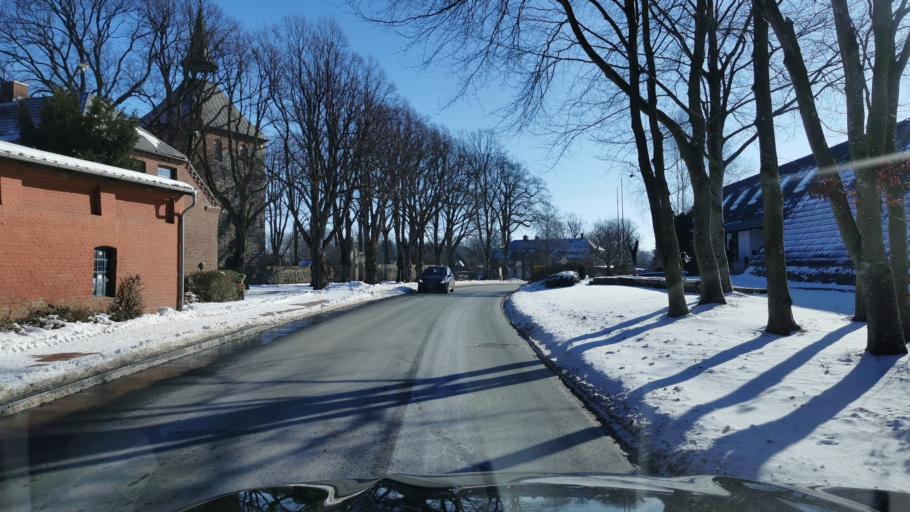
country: DE
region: Schleswig-Holstein
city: Grundhof
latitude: 54.7742
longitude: 9.6527
